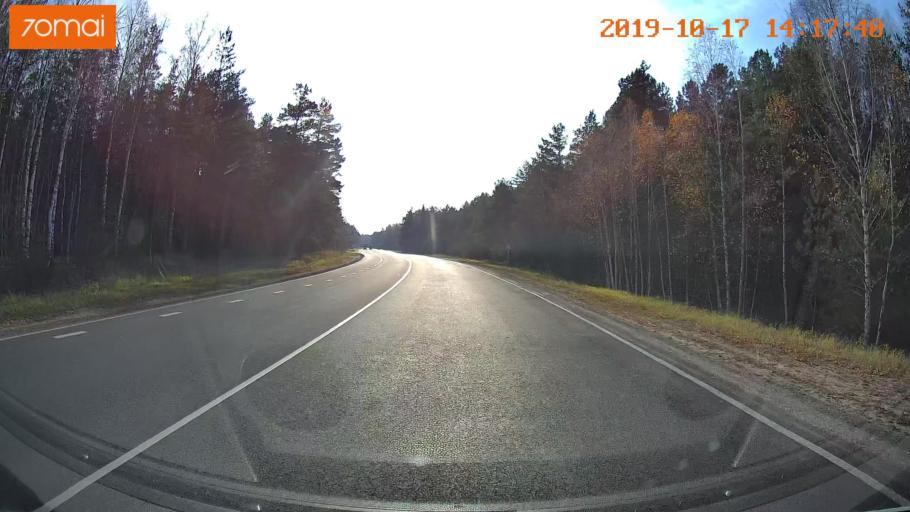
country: RU
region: Rjazan
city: Spas-Klepiki
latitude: 55.0727
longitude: 40.0381
